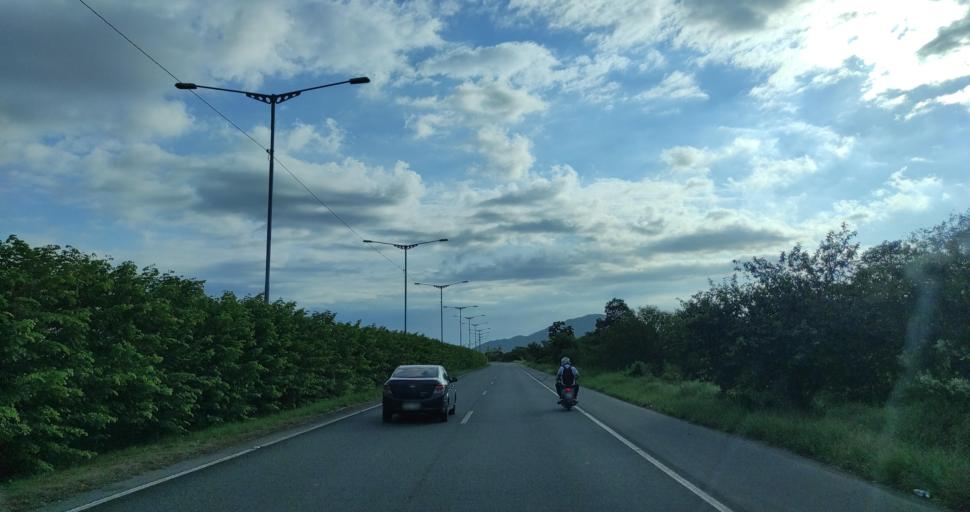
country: BR
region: Santa Catarina
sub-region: Penha
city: Penha
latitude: -26.8042
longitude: -48.6349
